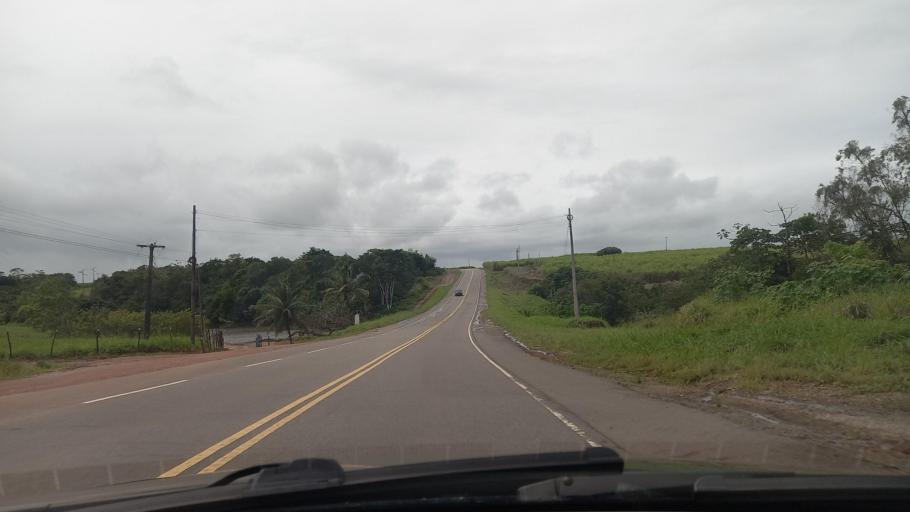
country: BR
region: Alagoas
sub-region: Sao Miguel Dos Campos
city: Sao Miguel dos Campos
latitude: -9.8046
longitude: -36.2050
